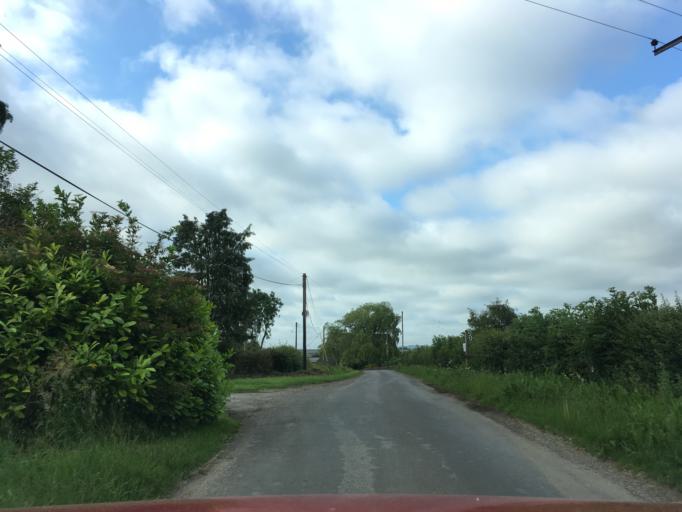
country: GB
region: England
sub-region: South Gloucestershire
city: Horton
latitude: 51.5616
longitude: -2.3519
